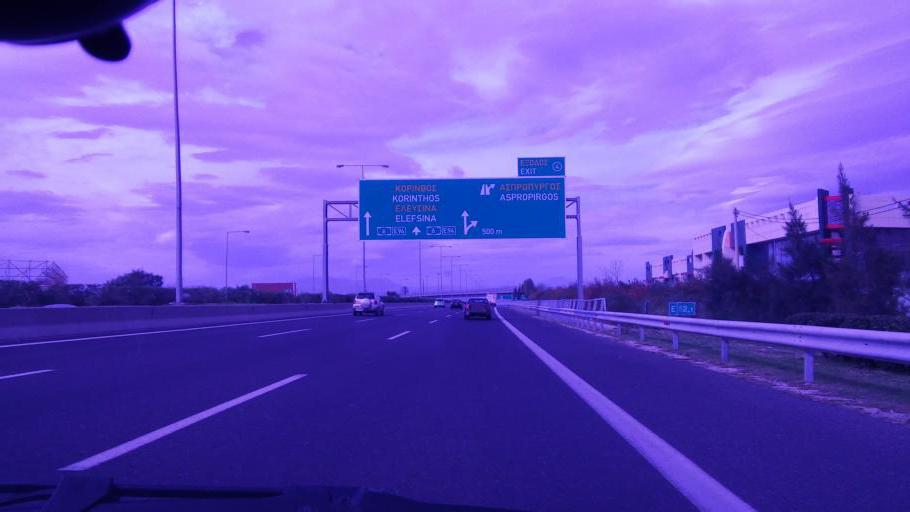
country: GR
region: Attica
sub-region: Nomarchia Dytikis Attikis
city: Fyli
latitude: 38.0879
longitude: 23.6310
